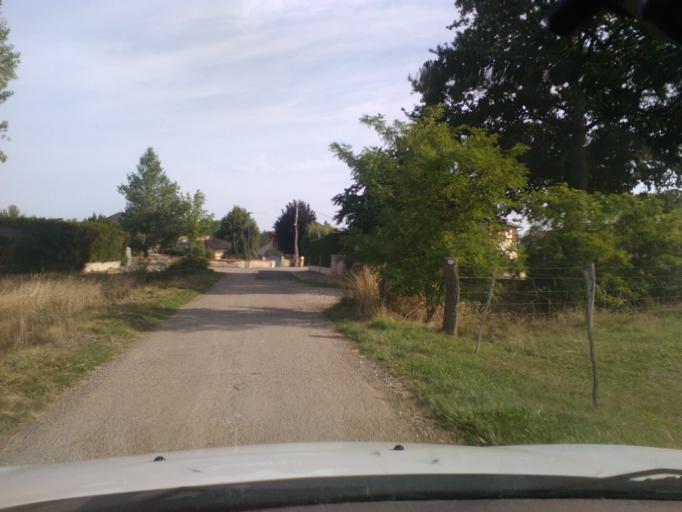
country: FR
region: Lorraine
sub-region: Departement des Vosges
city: Mirecourt
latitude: 48.3314
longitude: 6.0954
